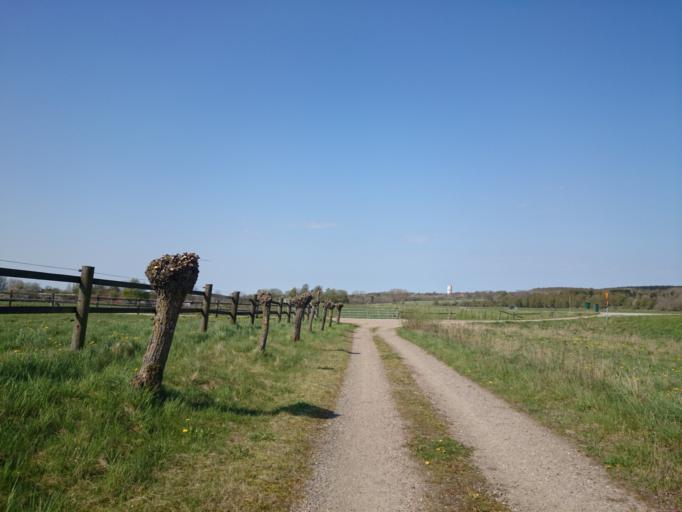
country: SE
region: Skane
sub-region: Lunds Kommun
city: Genarp
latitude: 55.6679
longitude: 13.3891
